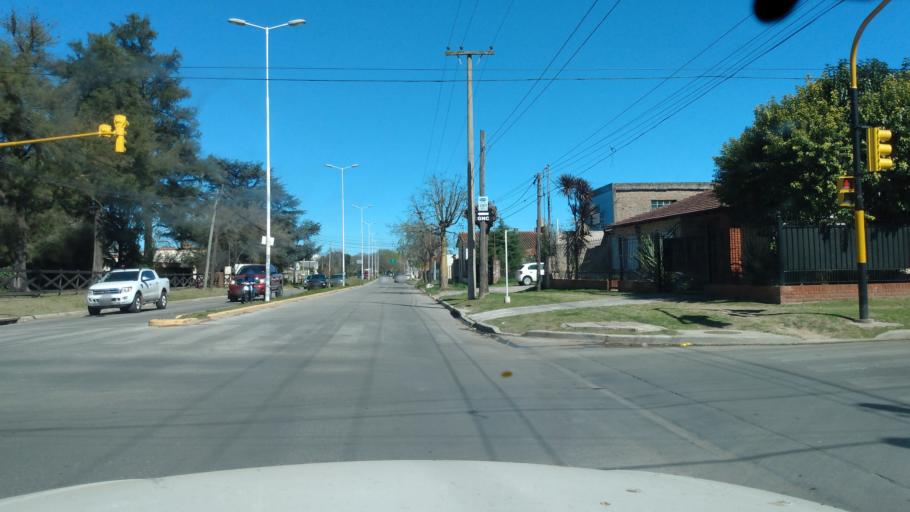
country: AR
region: Buenos Aires
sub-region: Partido de Lujan
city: Lujan
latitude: -34.5590
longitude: -59.1063
